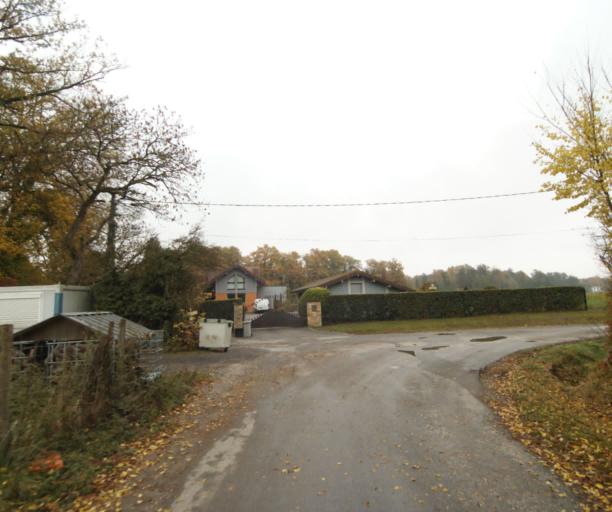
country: FR
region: Rhone-Alpes
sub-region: Departement de la Haute-Savoie
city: Bonne-sur-Menoge
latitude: 46.1382
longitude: 6.3028
